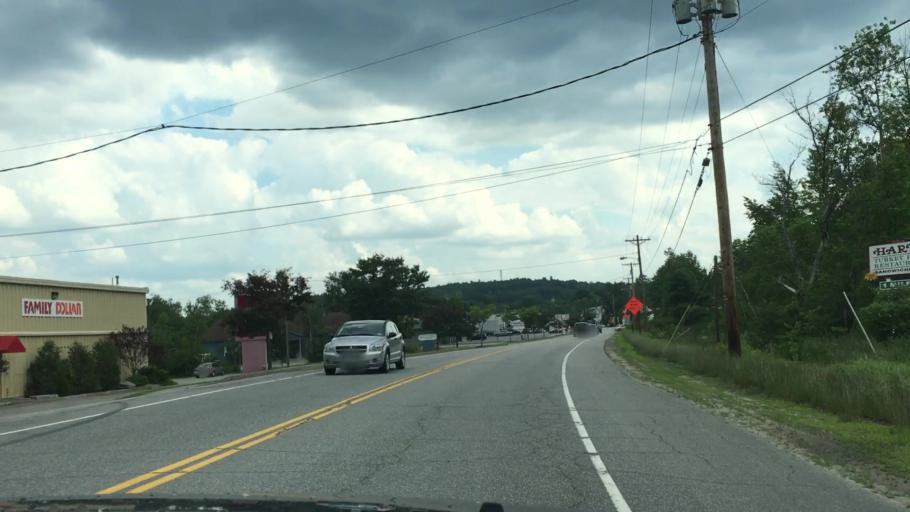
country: US
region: New Hampshire
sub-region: Belknap County
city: Meredith
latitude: 43.6635
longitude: -71.5009
